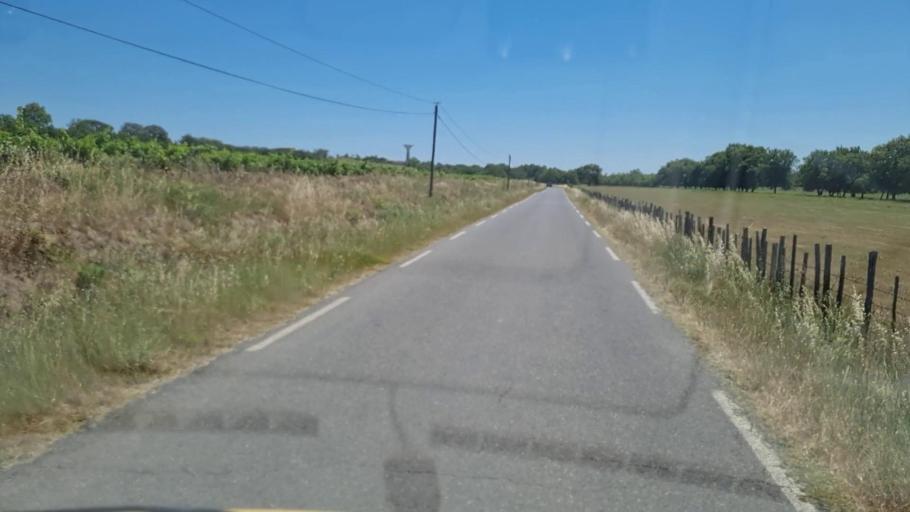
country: FR
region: Languedoc-Roussillon
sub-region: Departement du Gard
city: Le Cailar
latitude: 43.6500
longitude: 4.2521
